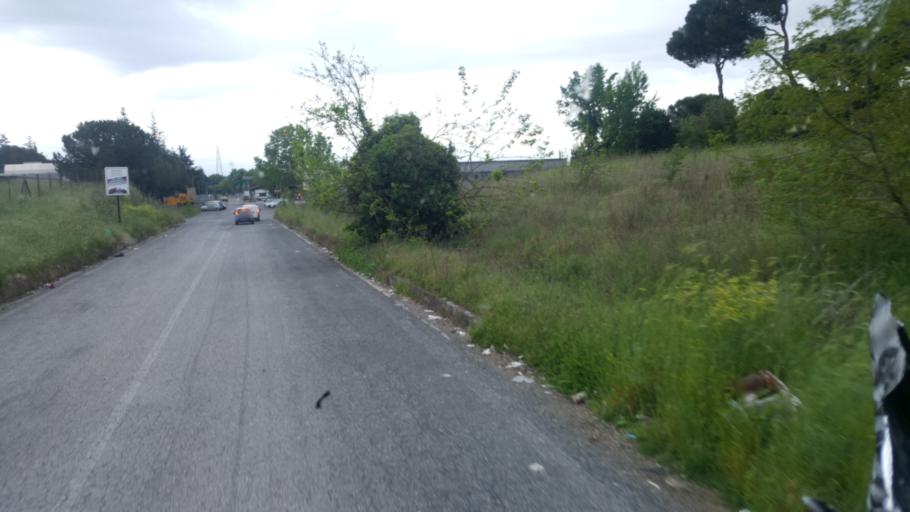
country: IT
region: Latium
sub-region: Citta metropolitana di Roma Capitale
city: Setteville
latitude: 41.9319
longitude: 12.6087
